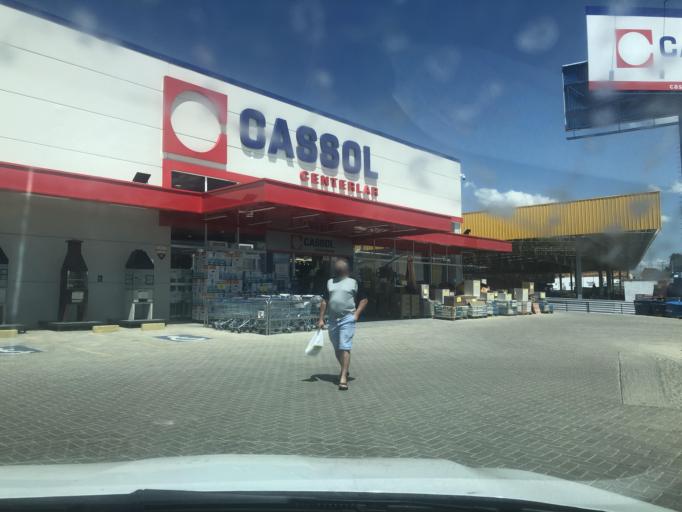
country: BR
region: Santa Catarina
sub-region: Lages
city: Lages
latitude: -27.7921
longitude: -50.2859
